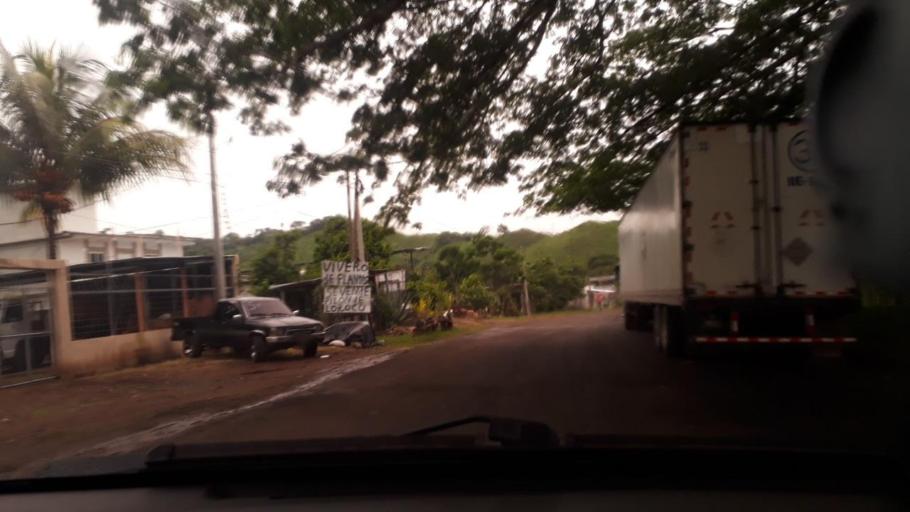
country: GT
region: Jutiapa
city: Atescatempa
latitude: 14.2261
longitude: -89.6981
